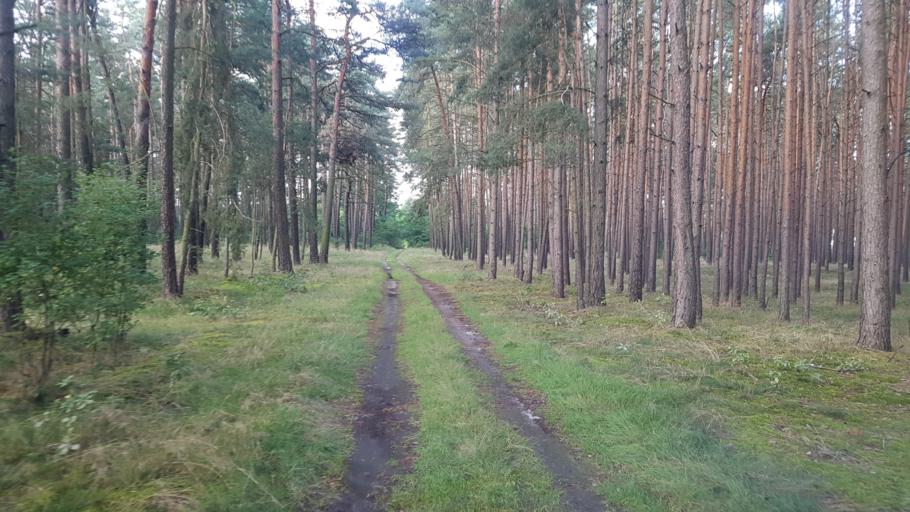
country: DE
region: Brandenburg
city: Schonewalde
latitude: 51.7034
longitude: 13.5792
